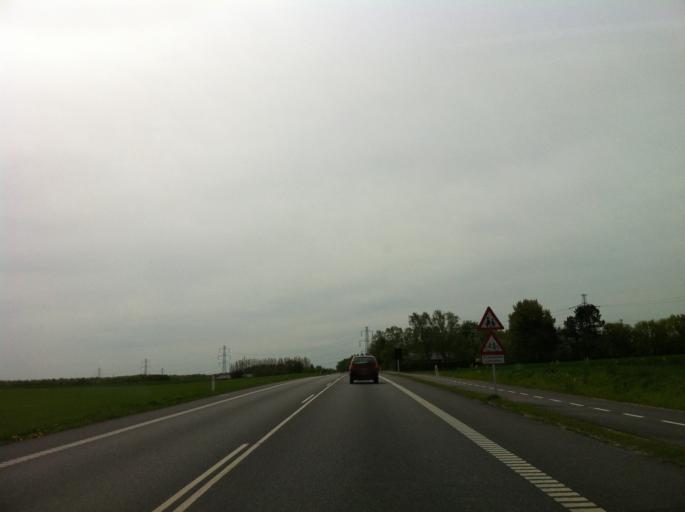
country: DK
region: Capital Region
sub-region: Egedal Kommune
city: Olstykke
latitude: 55.8198
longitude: 12.1655
